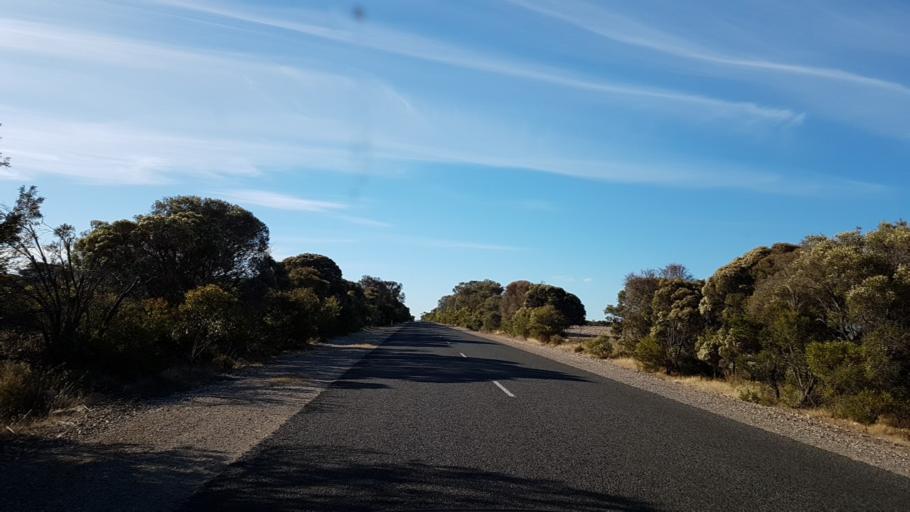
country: AU
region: South Australia
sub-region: Yorke Peninsula
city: Honiton
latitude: -34.9582
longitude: 137.1037
